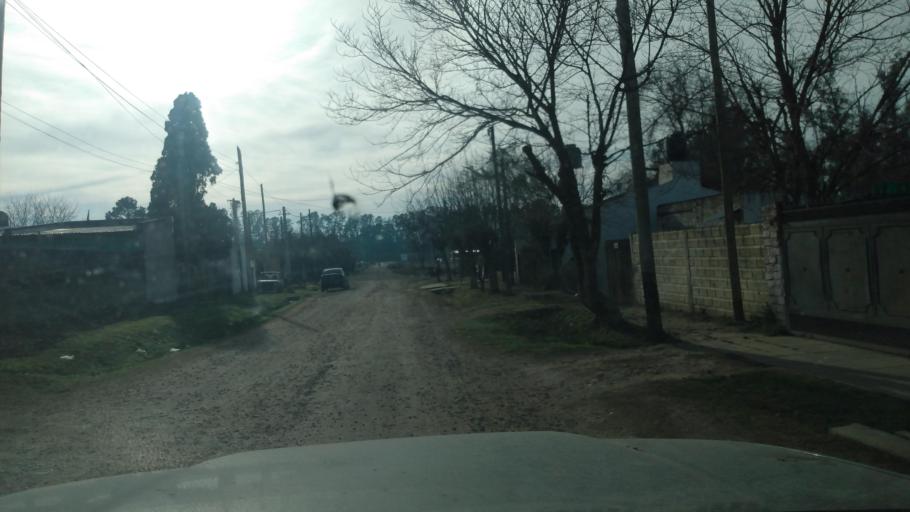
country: AR
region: Buenos Aires
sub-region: Partido de Lujan
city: Lujan
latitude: -34.5404
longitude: -59.1158
